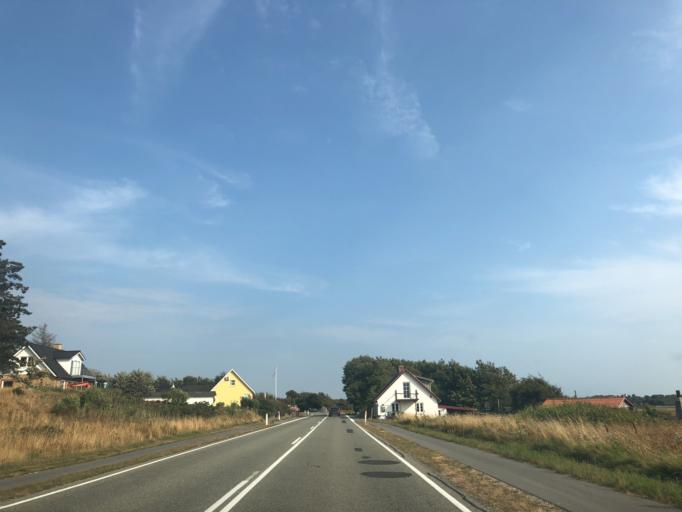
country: DK
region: North Denmark
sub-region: Morso Kommune
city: Nykobing Mors
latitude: 56.7961
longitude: 9.0349
